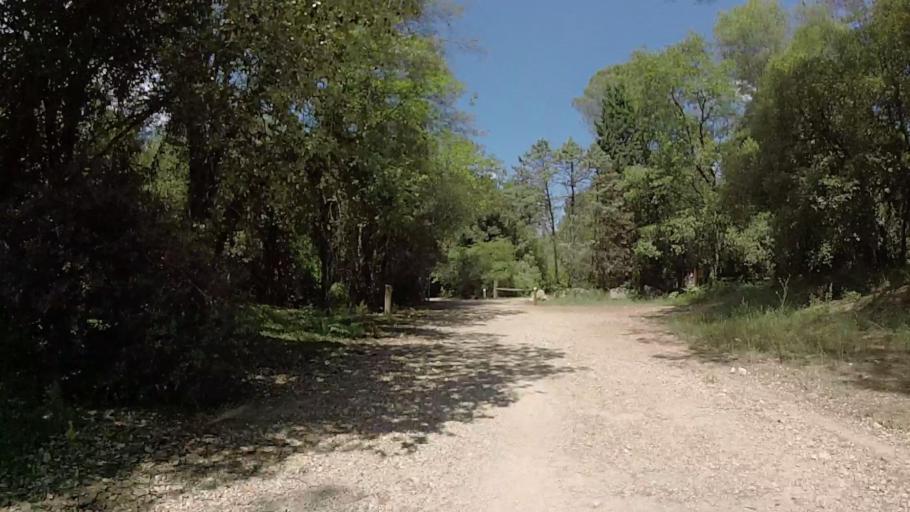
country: FR
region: Provence-Alpes-Cote d'Azur
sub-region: Departement des Alpes-Maritimes
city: Mougins
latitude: 43.5974
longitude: 7.0205
